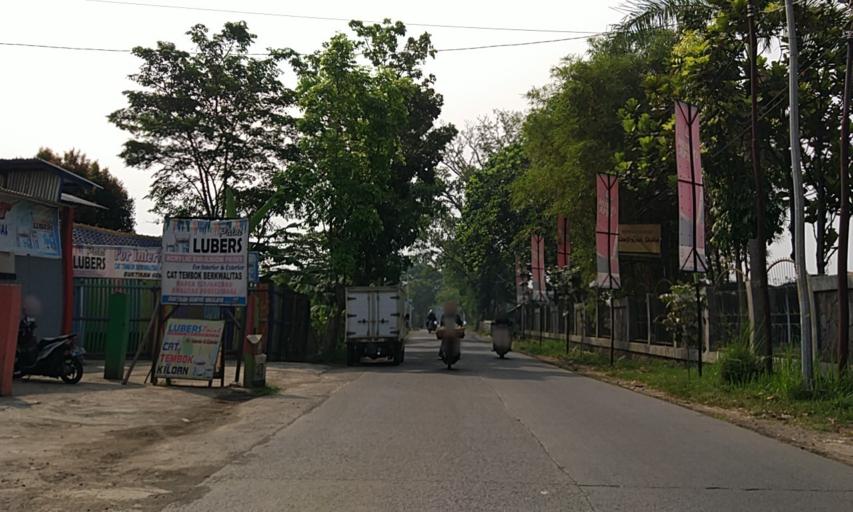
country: ID
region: West Java
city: Soreang
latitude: -7.0333
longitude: 107.5505
